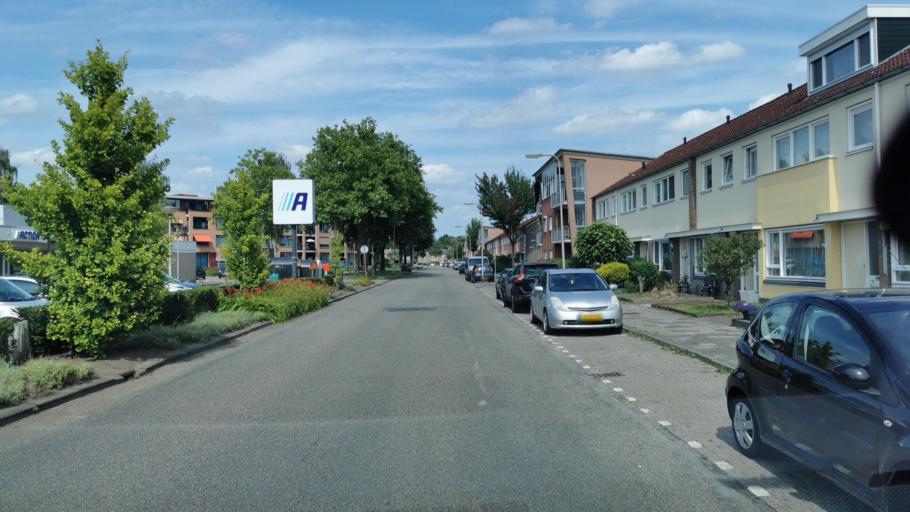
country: NL
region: Overijssel
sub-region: Gemeente Enschede
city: Enschede
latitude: 52.1863
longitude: 6.8830
